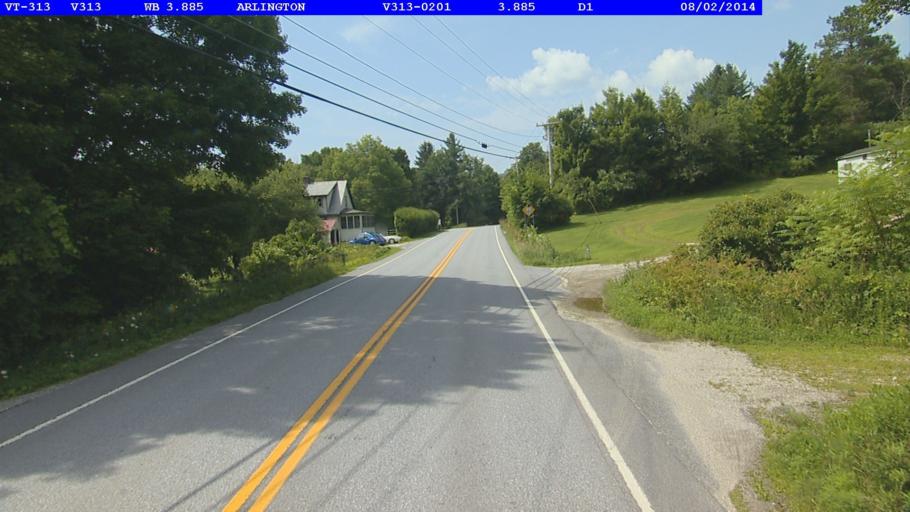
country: US
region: Vermont
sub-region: Bennington County
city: Arlington
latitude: 43.0926
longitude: -73.1987
